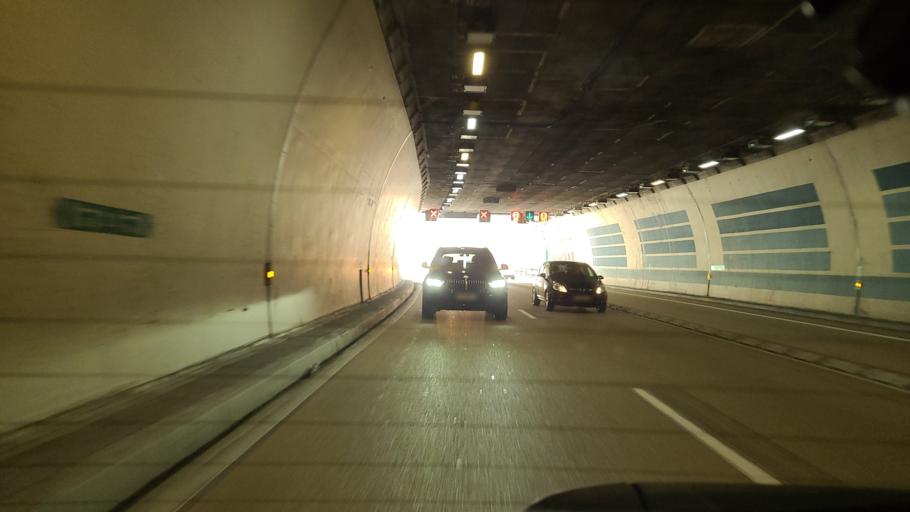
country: FR
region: Provence-Alpes-Cote d'Azur
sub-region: Departement des Alpes-Maritimes
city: La Turbie
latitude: 43.7343
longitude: 7.3868
